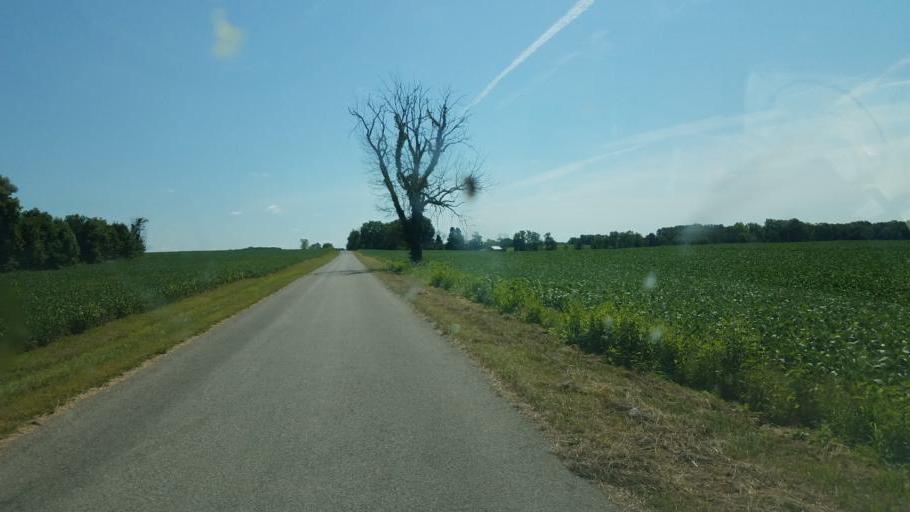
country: US
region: Ohio
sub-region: Morrow County
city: Mount Gilead
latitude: 40.4717
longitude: -82.6950
